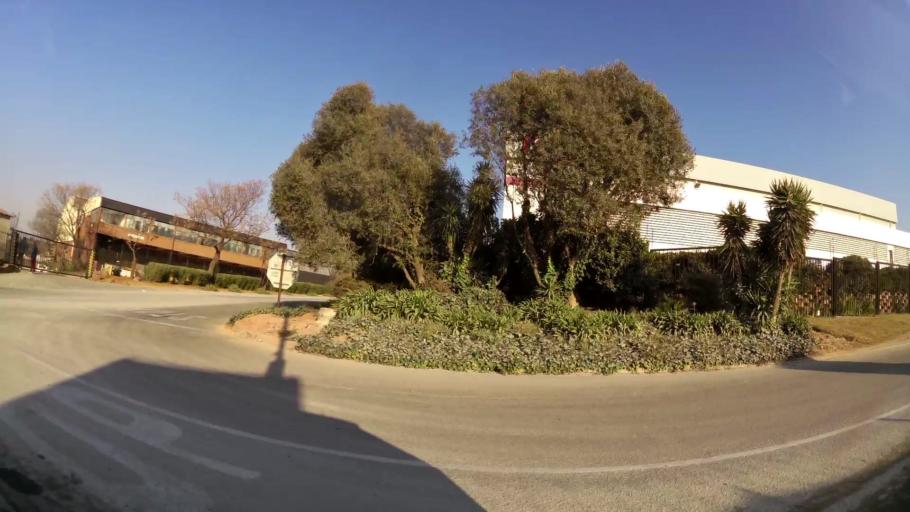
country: ZA
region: Gauteng
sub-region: City of Johannesburg Metropolitan Municipality
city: Modderfontein
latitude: -26.0847
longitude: 28.0908
